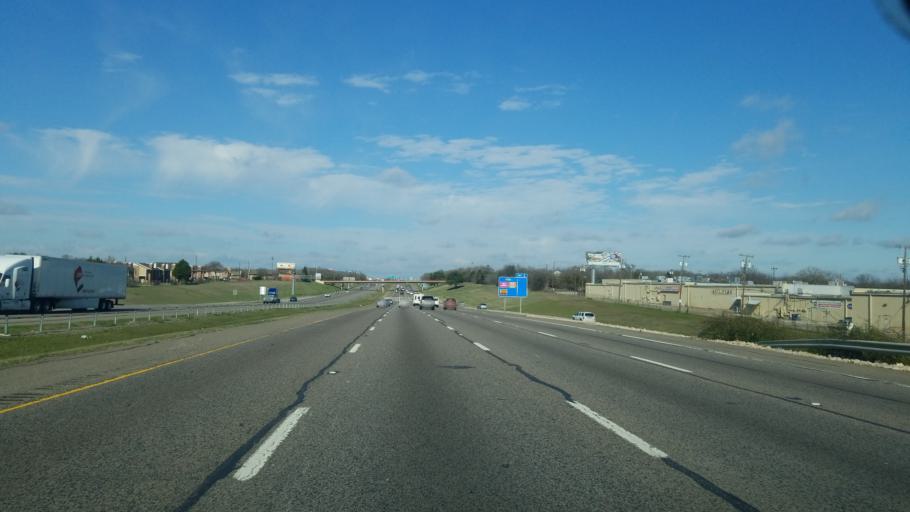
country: US
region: Texas
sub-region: Dallas County
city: Balch Springs
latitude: 32.7201
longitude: -96.6160
